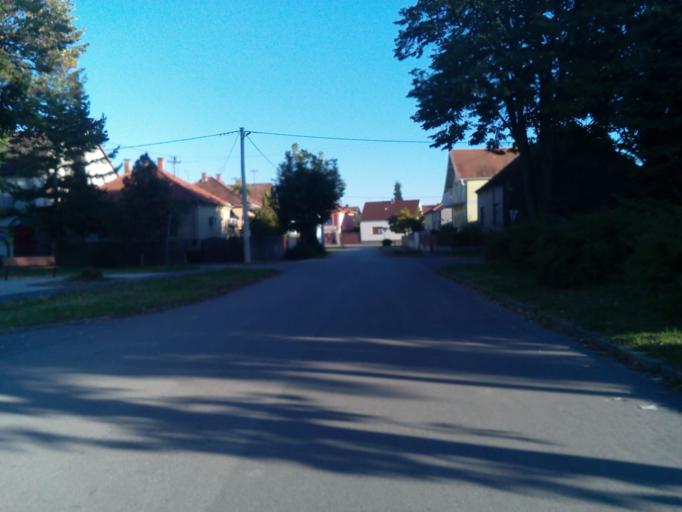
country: HR
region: Vukovarsko-Srijemska
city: Vinkovci
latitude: 45.2827
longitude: 18.8137
